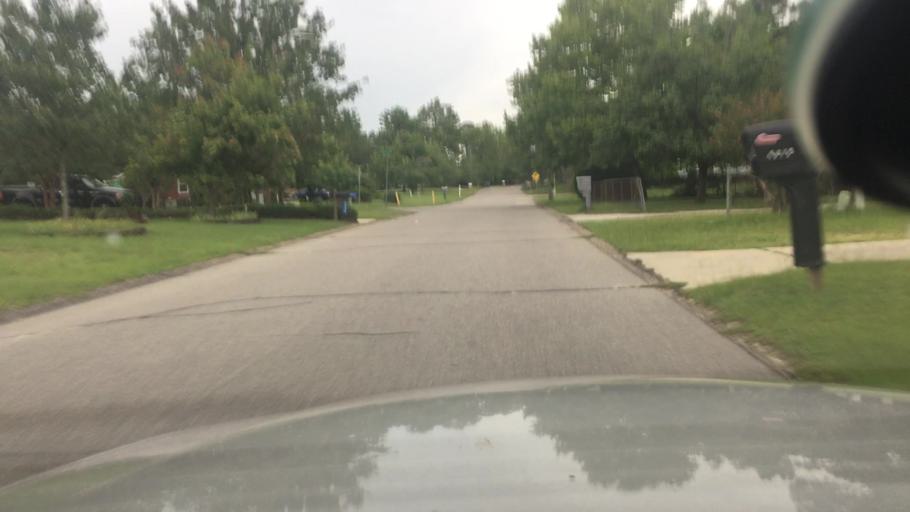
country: US
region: North Carolina
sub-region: Cumberland County
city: Hope Mills
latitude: 34.9711
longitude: -78.9753
